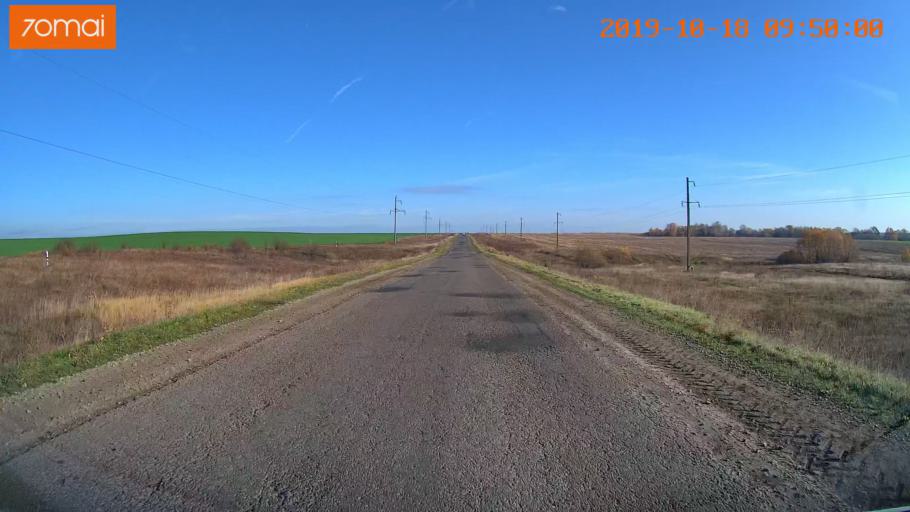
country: RU
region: Tula
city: Kazachka
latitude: 53.3240
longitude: 38.2713
